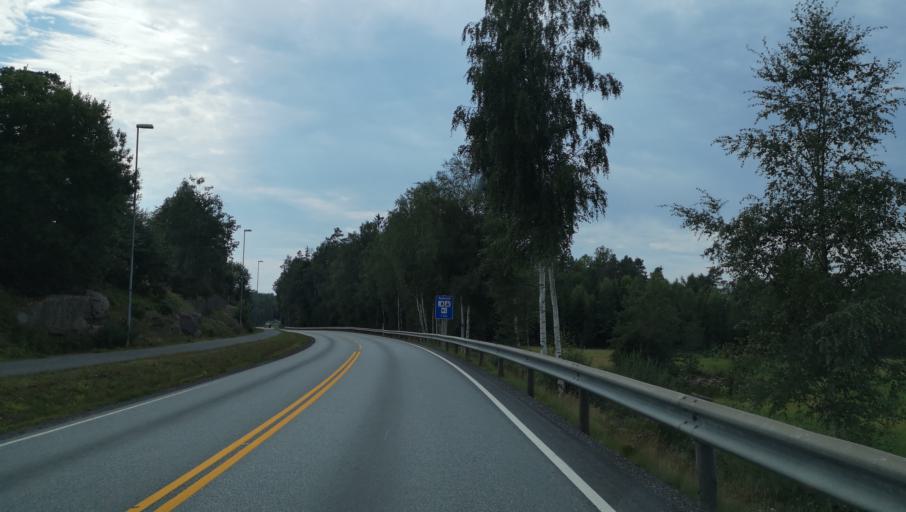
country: NO
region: Ostfold
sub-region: Rygge
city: Rygge
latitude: 59.4677
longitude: 10.7806
